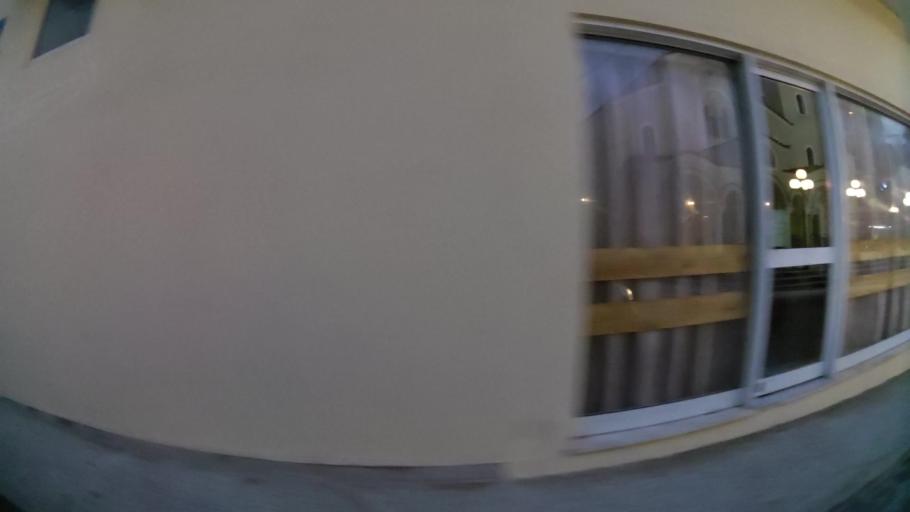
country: GR
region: Attica
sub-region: Nomarchia Anatolikis Attikis
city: Spata
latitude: 37.9621
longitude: 23.9109
